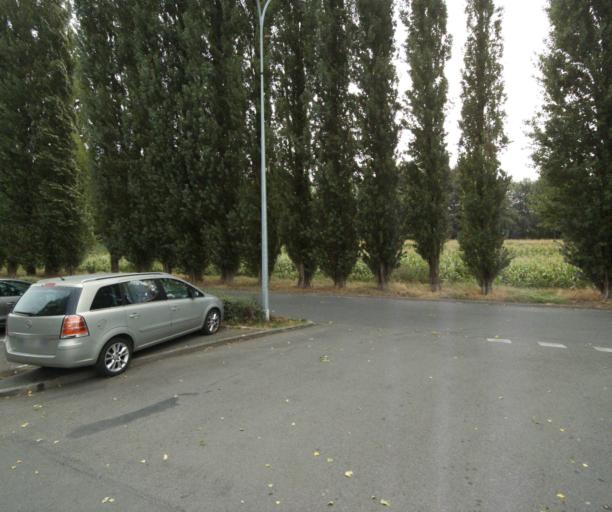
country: FR
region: Nord-Pas-de-Calais
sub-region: Departement du Nord
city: Emmerin
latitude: 50.6063
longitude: 3.0061
